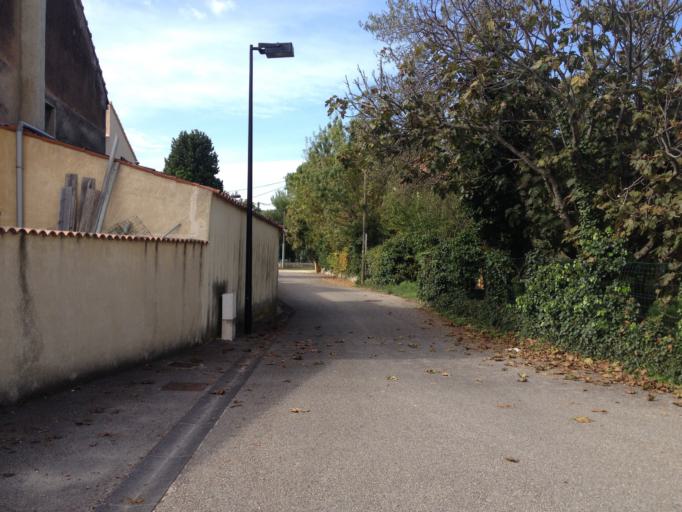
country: FR
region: Provence-Alpes-Cote d'Azur
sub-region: Departement du Vaucluse
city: Orange
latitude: 44.1310
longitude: 4.8215
